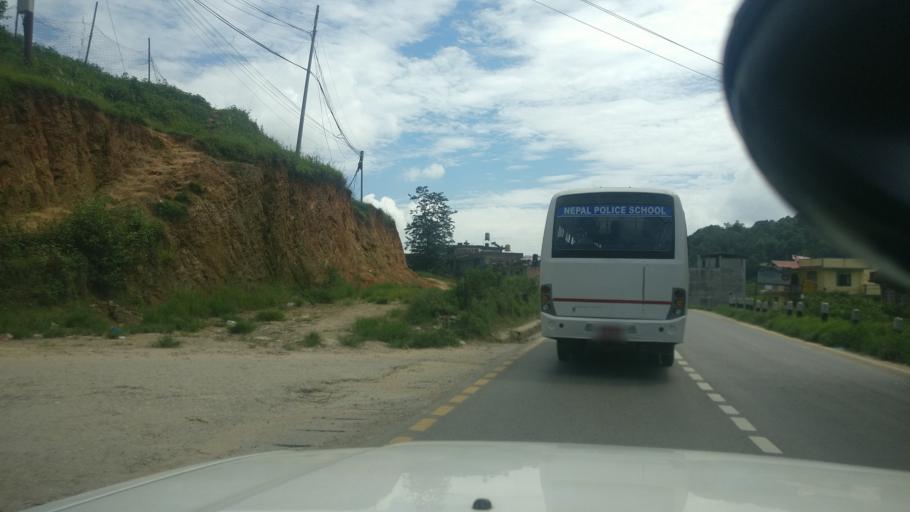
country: NP
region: Central Region
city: Banepa
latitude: 27.6321
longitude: 85.4989
